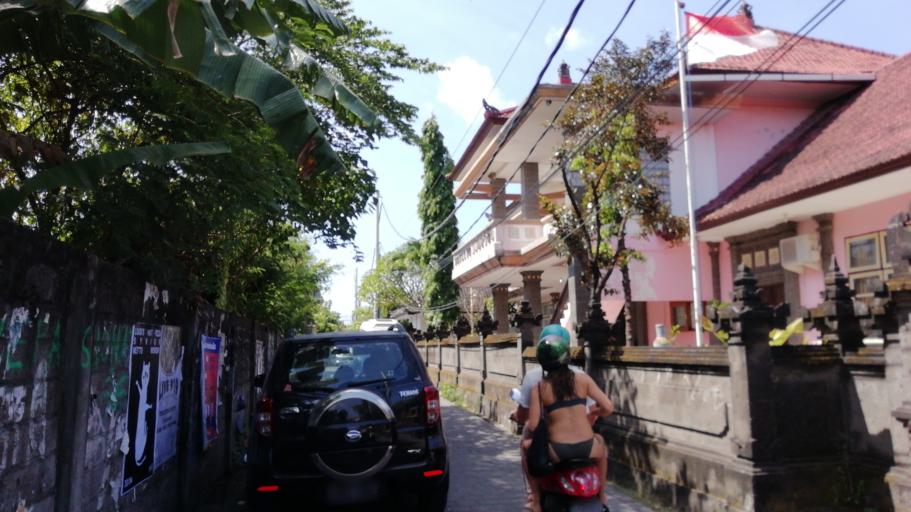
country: ID
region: Bali
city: Banjar Kerobokan
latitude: -8.6545
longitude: 115.1405
